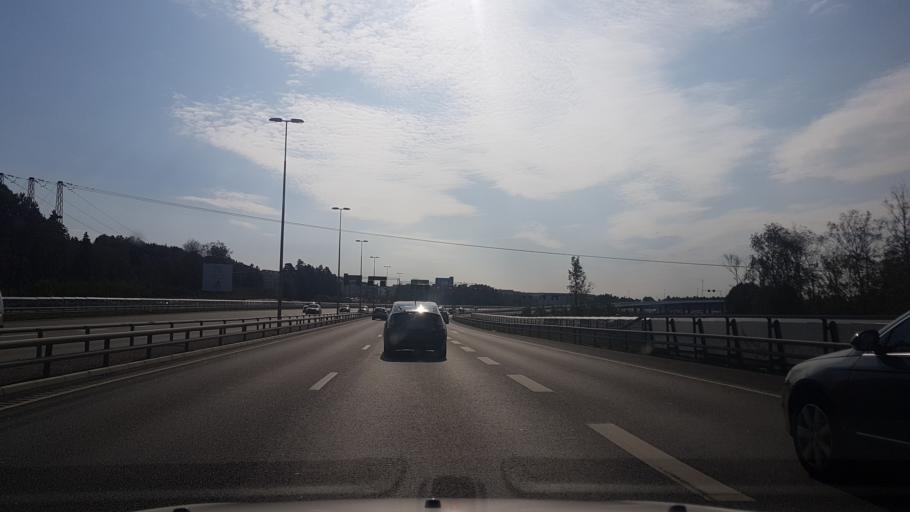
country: SE
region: Stockholm
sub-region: Stockholms Kommun
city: Kista
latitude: 59.3928
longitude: 17.9486
